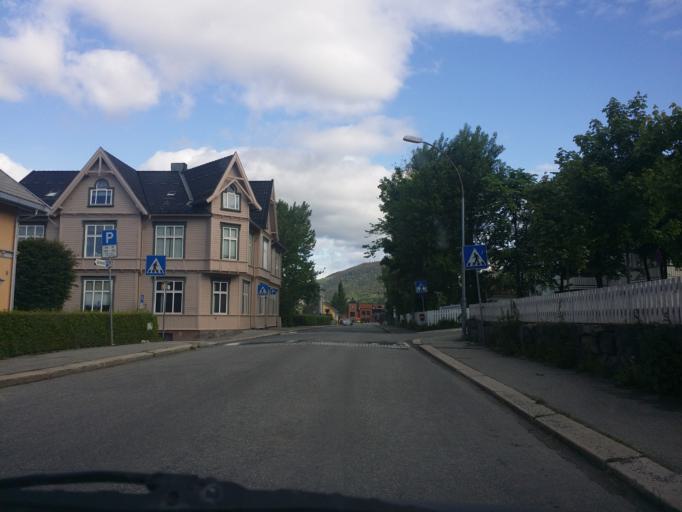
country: NO
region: Oppland
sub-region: Lillehammer
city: Lillehammer
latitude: 61.1143
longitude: 10.4697
